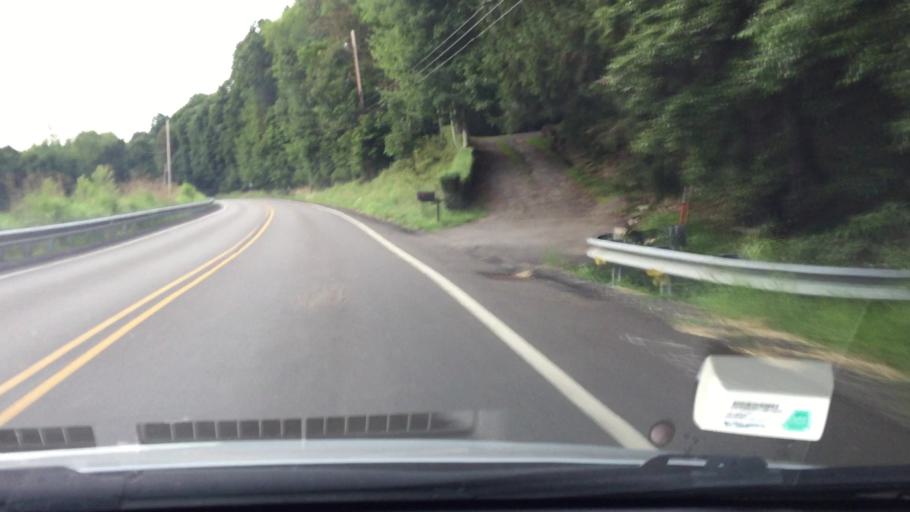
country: US
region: Pennsylvania
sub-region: Allegheny County
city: Gibsonia
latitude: 40.6309
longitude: -80.0247
